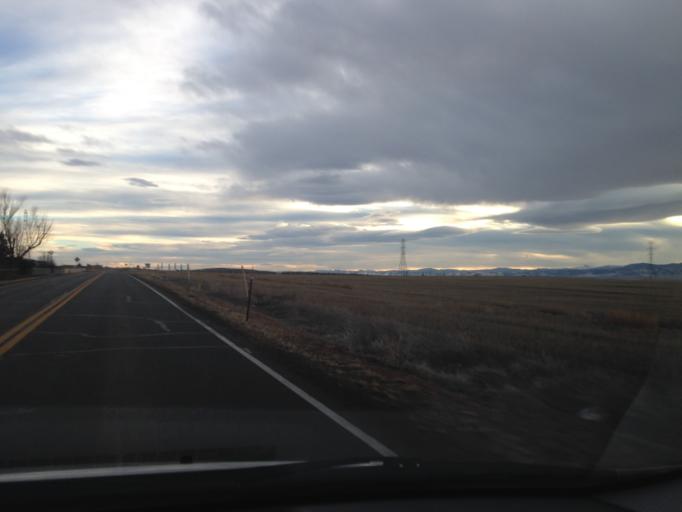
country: US
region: Colorado
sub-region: Boulder County
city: Erie
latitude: 40.0626
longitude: -105.0182
